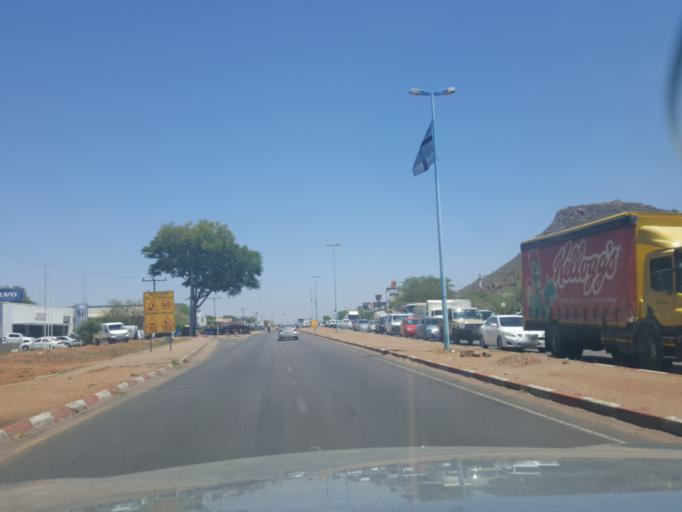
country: BW
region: South East
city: Gaborone
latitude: -24.6877
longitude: 25.8831
